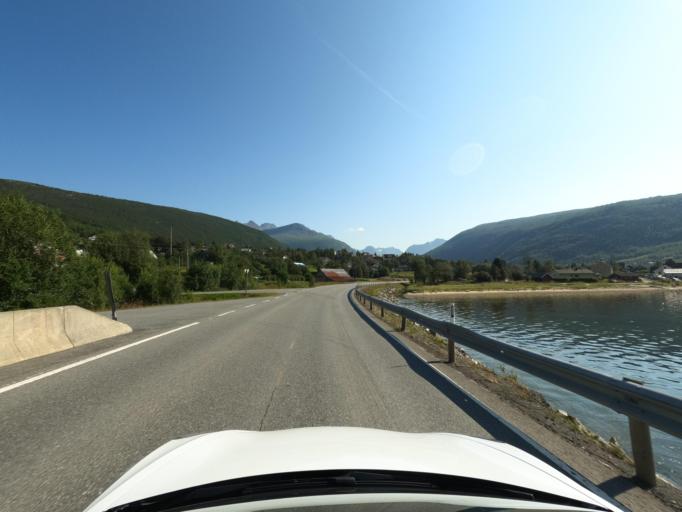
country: NO
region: Nordland
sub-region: Narvik
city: Bjerkvik
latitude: 68.3794
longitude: 17.5976
